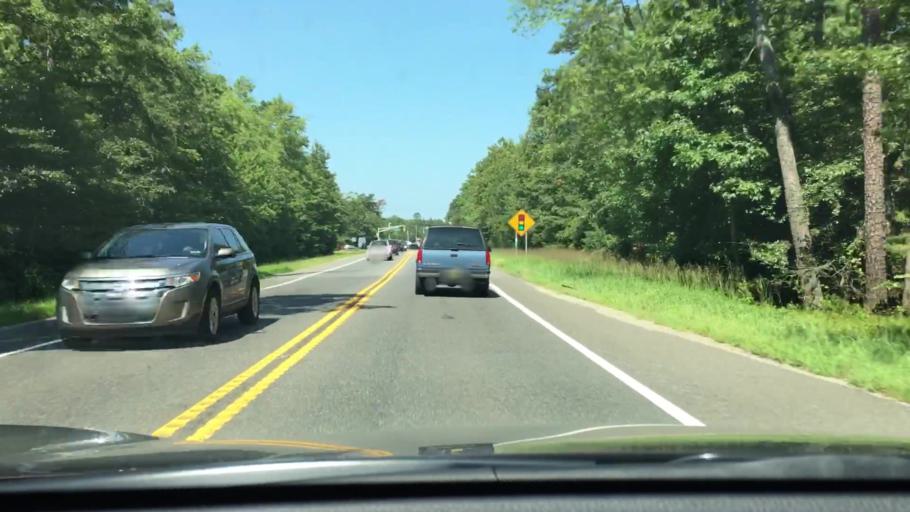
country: US
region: New Jersey
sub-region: Cumberland County
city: Laurel Lake
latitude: 39.2897
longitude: -74.9642
